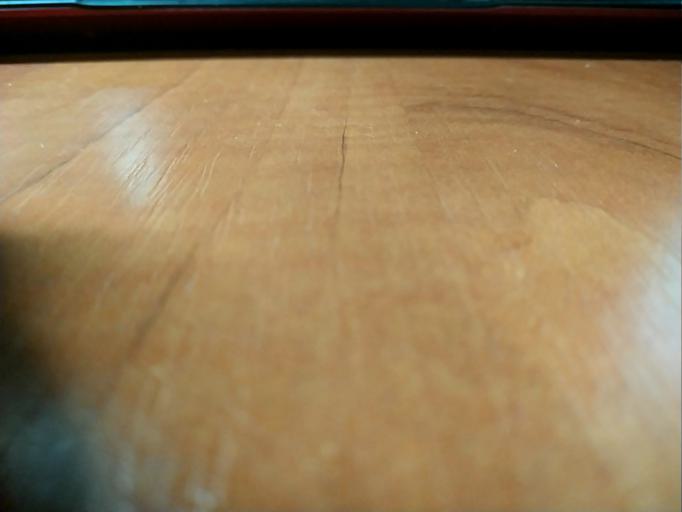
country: RU
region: Tverskaya
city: Ves'yegonsk
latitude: 58.7254
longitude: 37.5439
